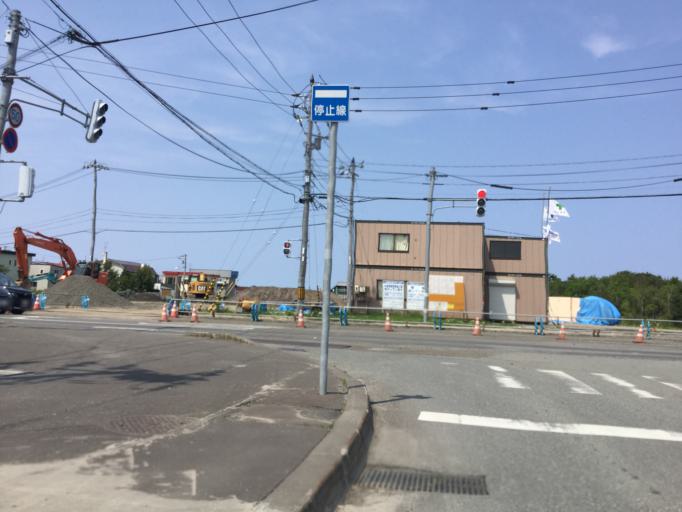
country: JP
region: Hokkaido
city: Wakkanai
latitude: 45.3864
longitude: 141.7042
